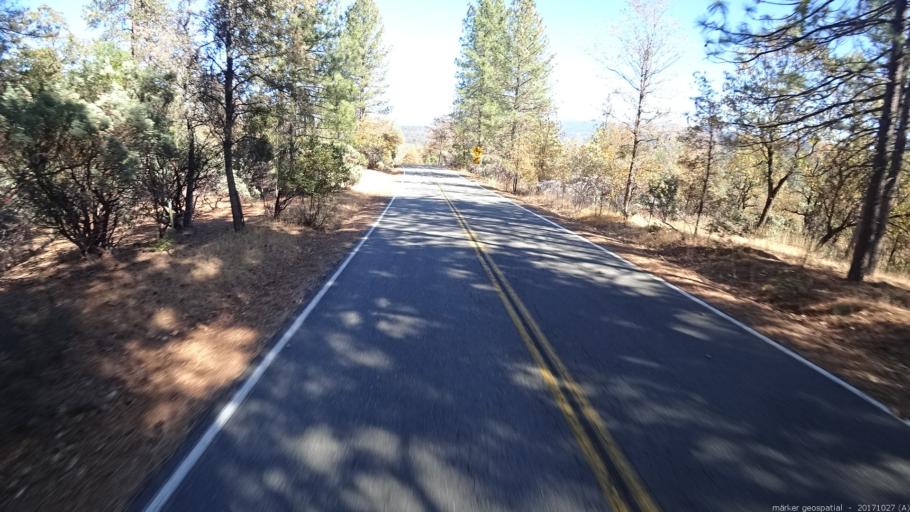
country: US
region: California
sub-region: Shasta County
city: Bella Vista
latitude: 40.7291
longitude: -122.0149
